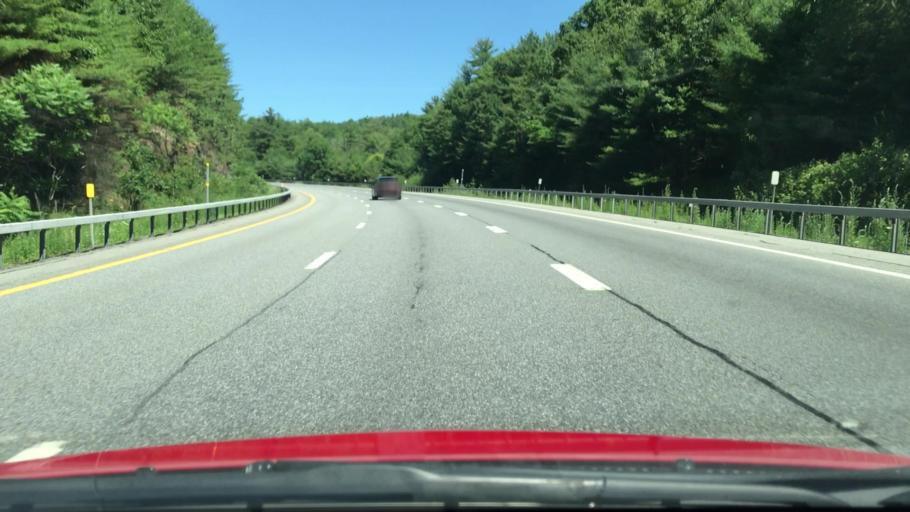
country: US
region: New York
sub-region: Warren County
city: Warrensburg
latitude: 43.4579
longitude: -73.7364
